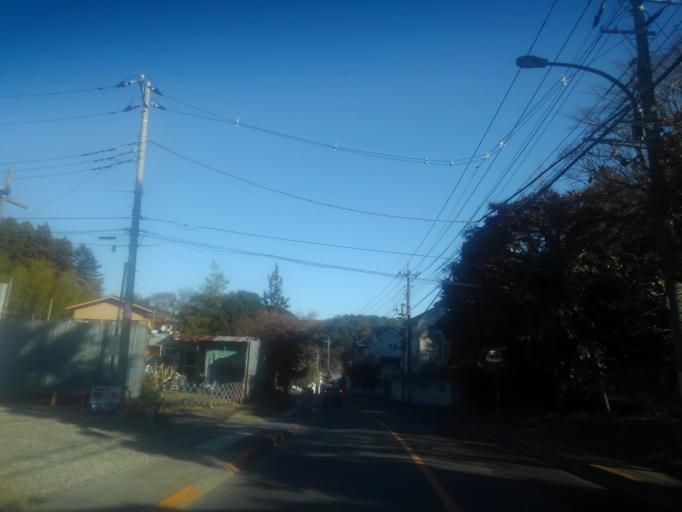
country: JP
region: Tokyo
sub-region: Machida-shi
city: Machida
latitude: 35.5951
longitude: 139.4370
